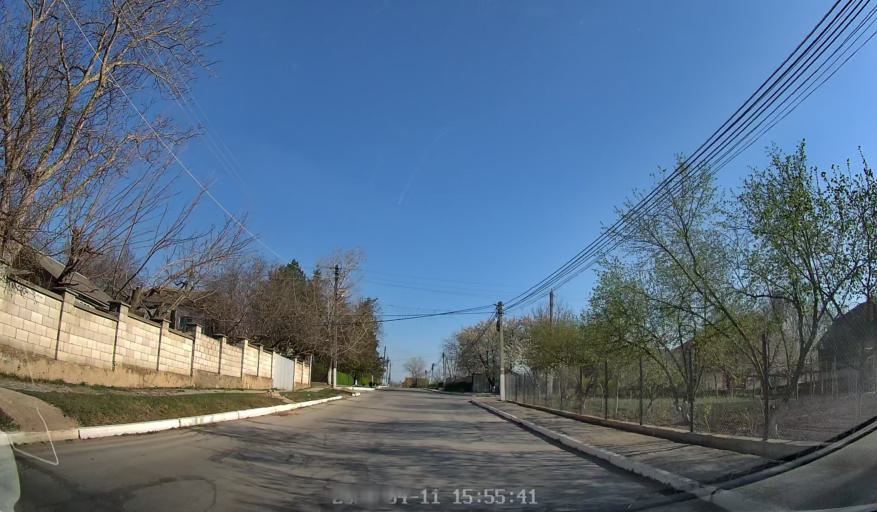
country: MD
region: Chisinau
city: Vadul lui Voda
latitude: 47.0949
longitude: 29.1774
